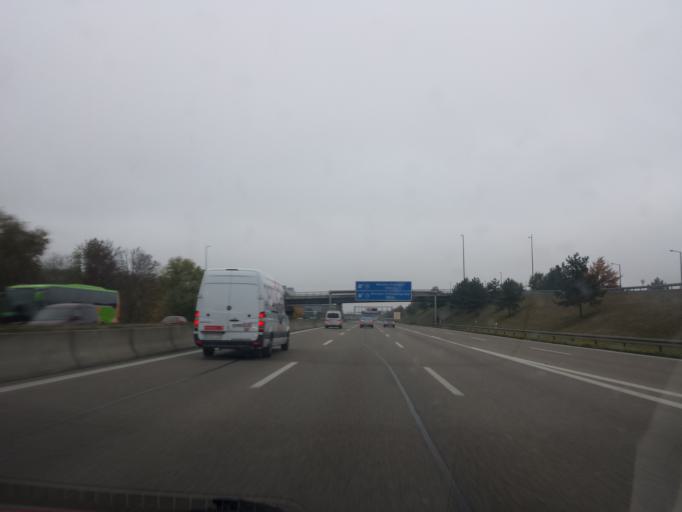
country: DE
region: Bavaria
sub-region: Upper Bavaria
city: Unterfoehring
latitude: 48.2183
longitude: 11.6278
